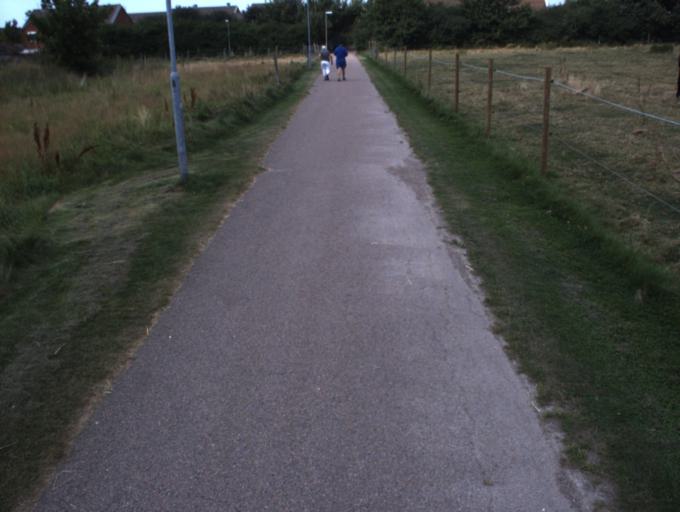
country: SE
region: Skane
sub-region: Helsingborg
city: Helsingborg
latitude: 56.0929
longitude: 12.6604
